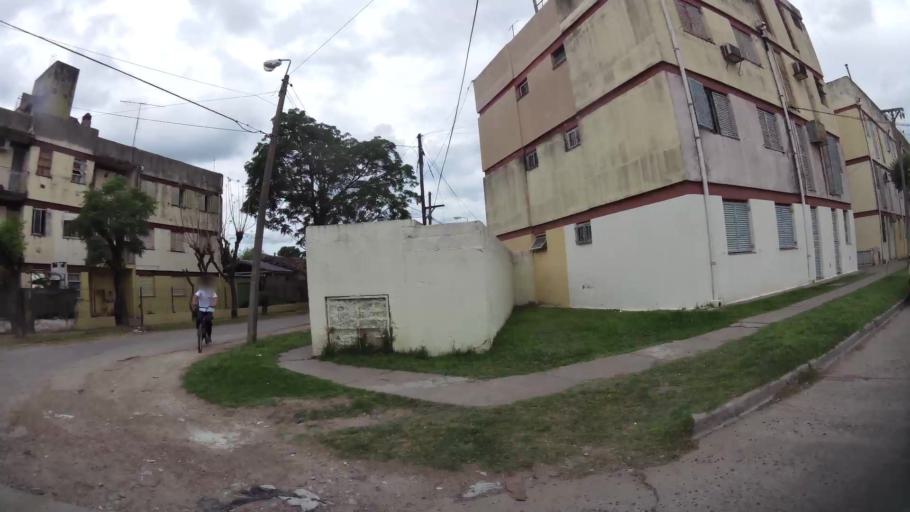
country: AR
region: Buenos Aires
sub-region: Partido de Zarate
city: Zarate
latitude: -34.1155
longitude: -59.0162
